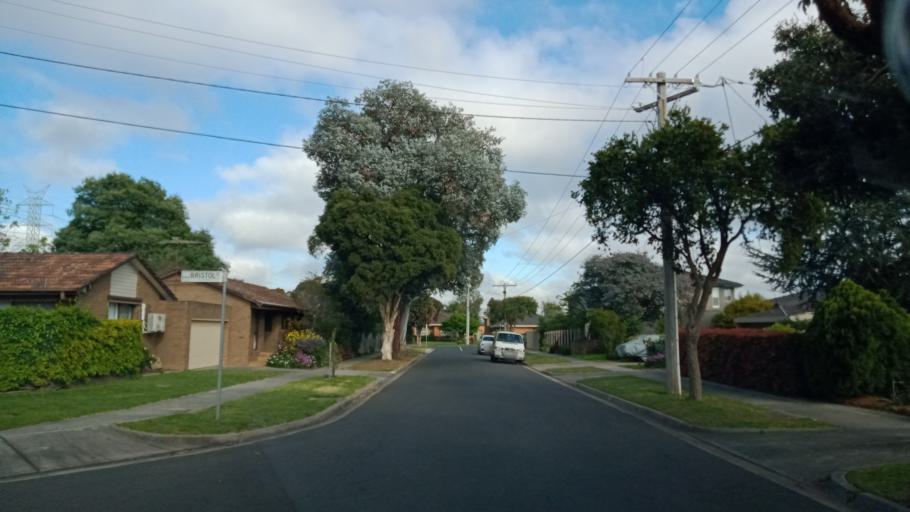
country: AU
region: Victoria
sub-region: Monash
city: Notting Hill
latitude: -37.8920
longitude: 145.1470
